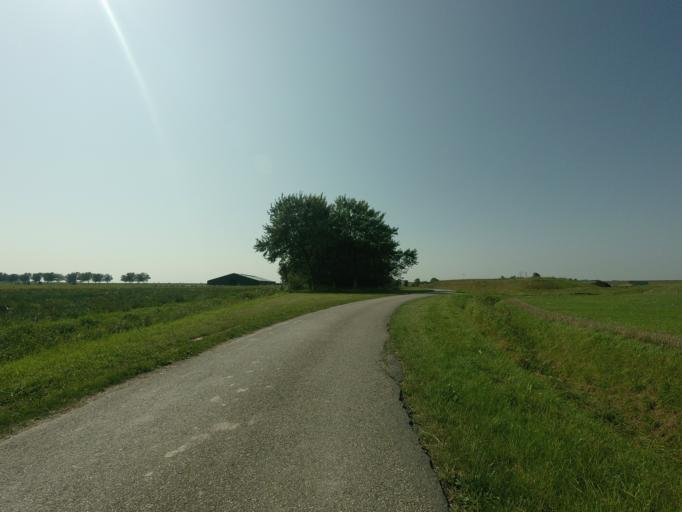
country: NL
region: Groningen
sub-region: Gemeente De Marne
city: Ulrum
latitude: 53.3672
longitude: 6.2840
